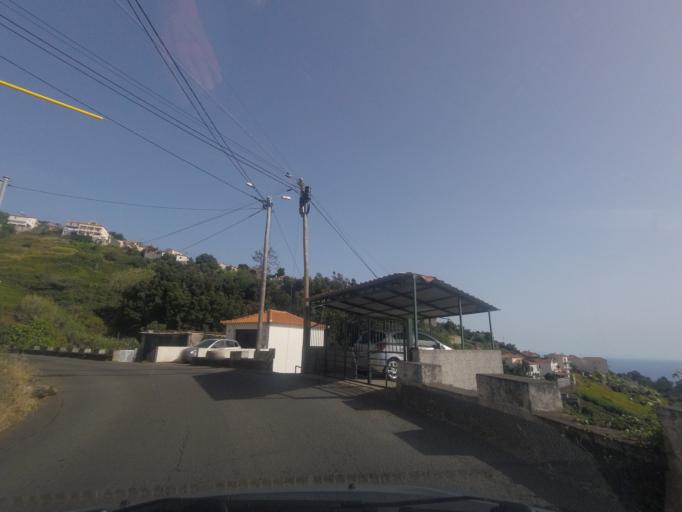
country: PT
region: Madeira
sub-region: Calheta
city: Arco da Calheta
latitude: 32.7288
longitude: -17.1534
